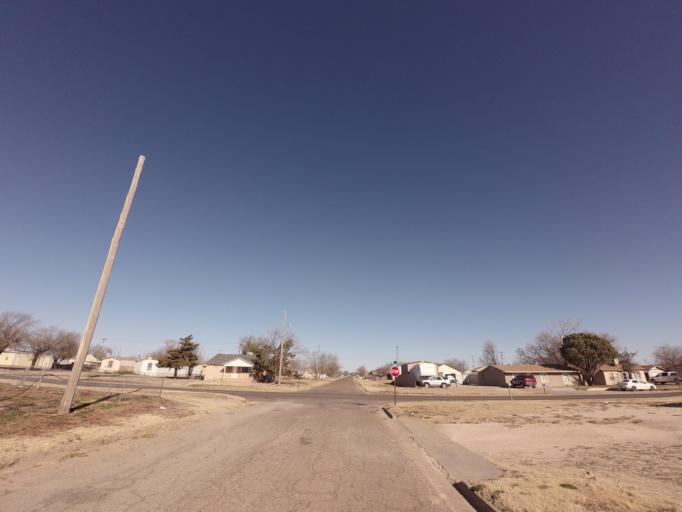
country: US
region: New Mexico
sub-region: Curry County
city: Clovis
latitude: 34.4005
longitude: -103.1940
